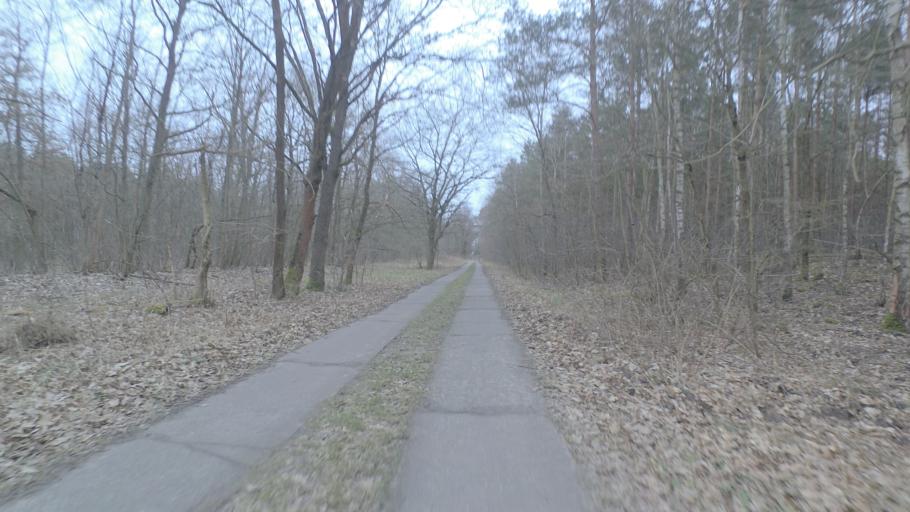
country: DE
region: Brandenburg
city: Ludwigsfelde
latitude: 52.3342
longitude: 13.2265
